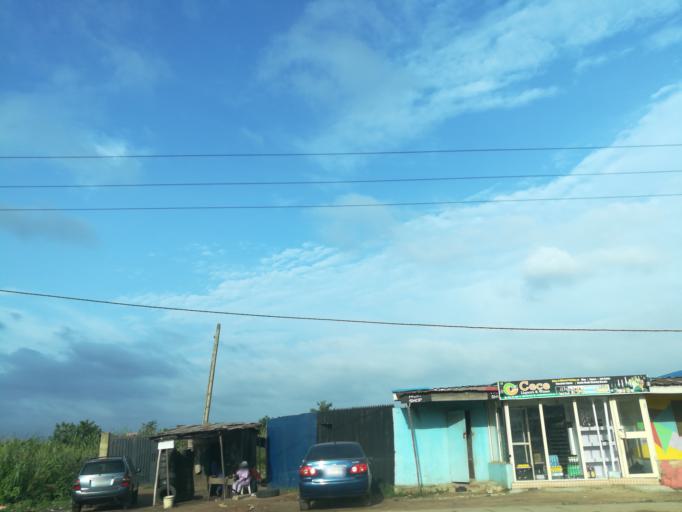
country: NG
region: Lagos
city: Ebute Ikorodu
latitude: 6.6076
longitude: 3.4846
